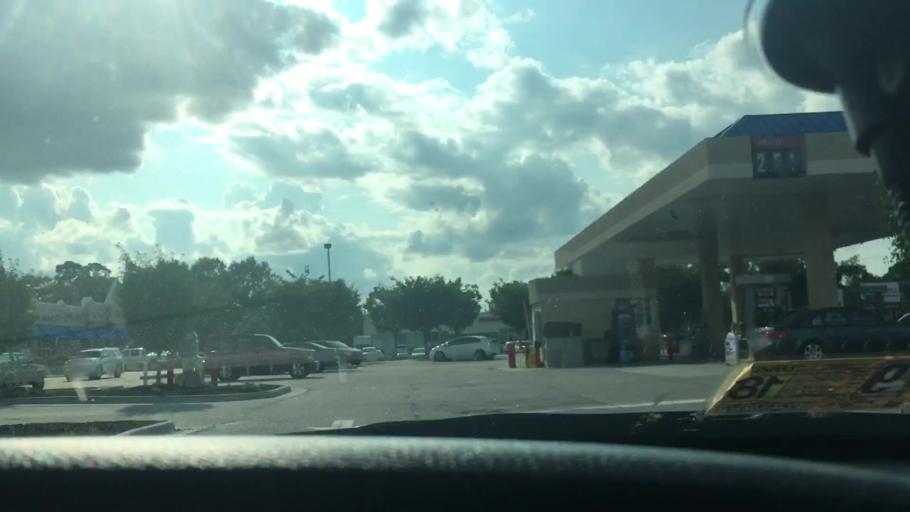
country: US
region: Virginia
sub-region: City of Norfolk
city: Norfolk
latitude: 36.9032
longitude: -76.1332
